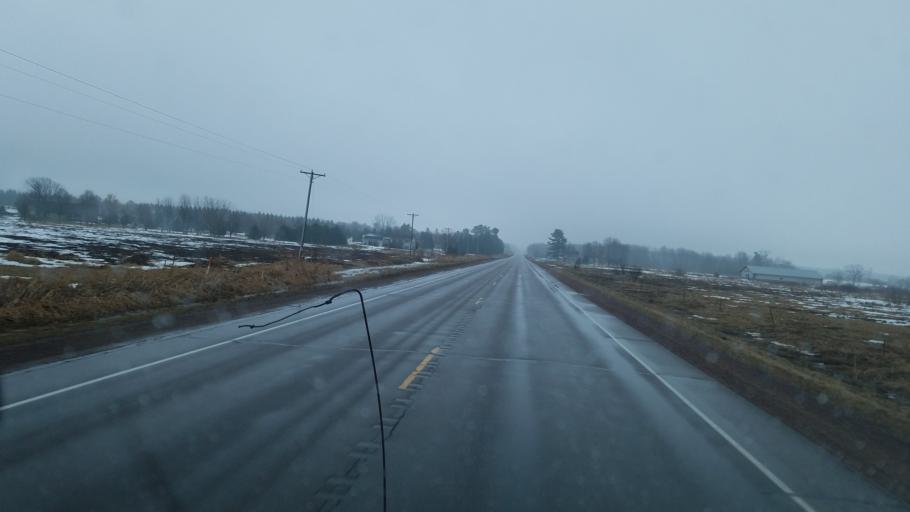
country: US
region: Wisconsin
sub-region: Wood County
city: Marshfield
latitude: 44.5986
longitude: -90.2307
